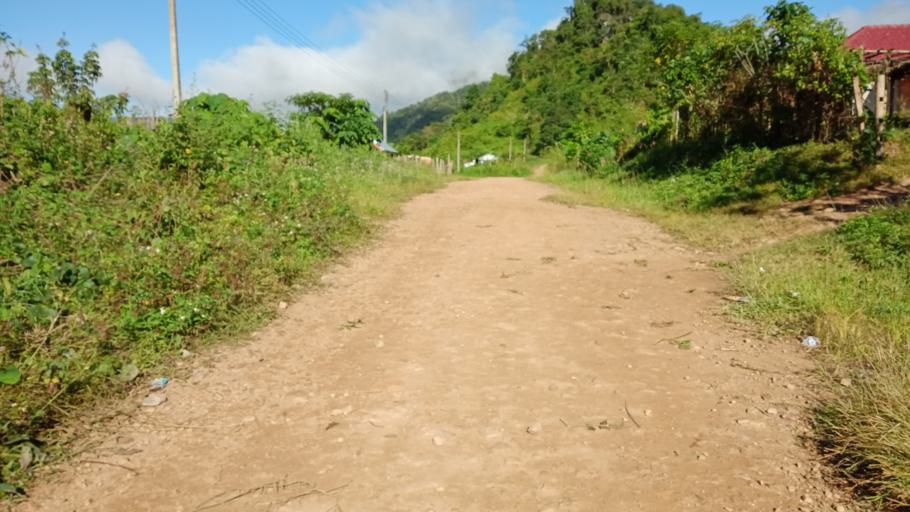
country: LA
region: Xiangkhoang
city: Phonsavan
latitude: 19.1159
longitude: 102.9109
